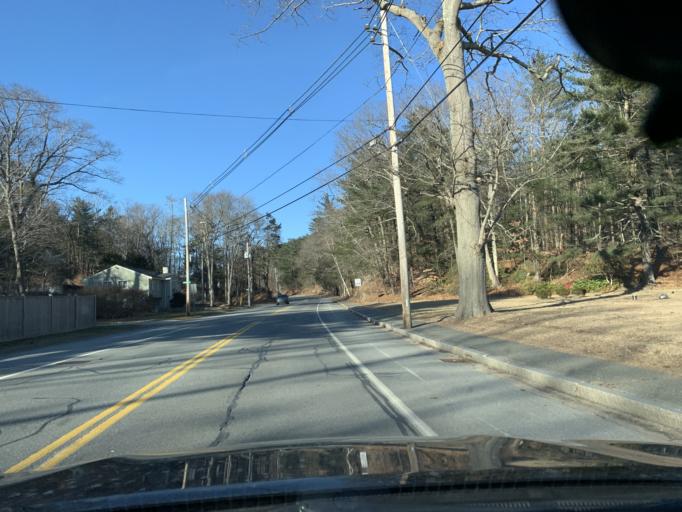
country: US
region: Massachusetts
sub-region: Essex County
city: Essex
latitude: 42.5839
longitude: -70.7810
